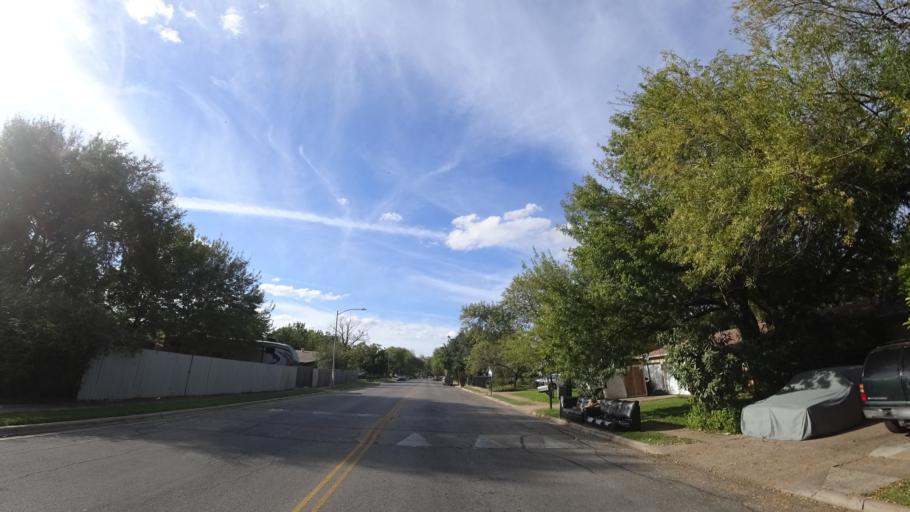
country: US
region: Texas
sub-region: Travis County
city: Onion Creek
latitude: 30.1887
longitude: -97.7545
